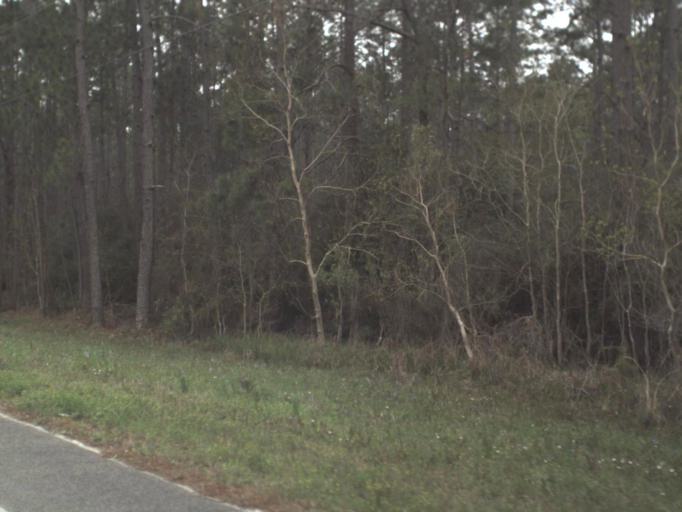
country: US
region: Florida
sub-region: Gulf County
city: Wewahitchka
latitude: 29.9524
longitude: -85.1806
